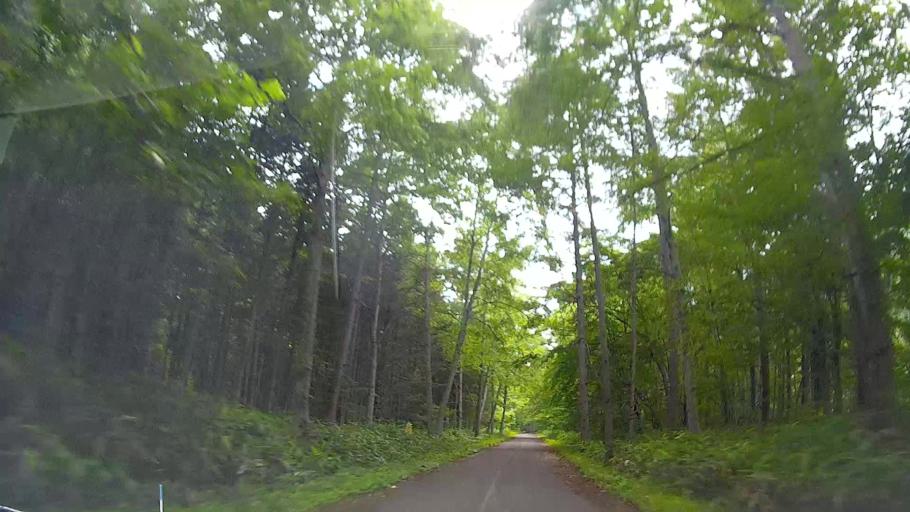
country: JP
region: Hokkaido
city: Nanae
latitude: 42.0534
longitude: 140.4965
